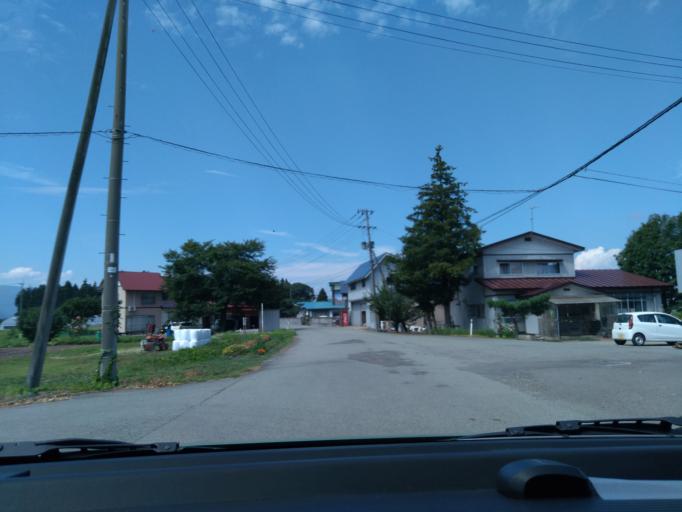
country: JP
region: Akita
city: Kakunodatemachi
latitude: 39.6097
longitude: 140.5944
